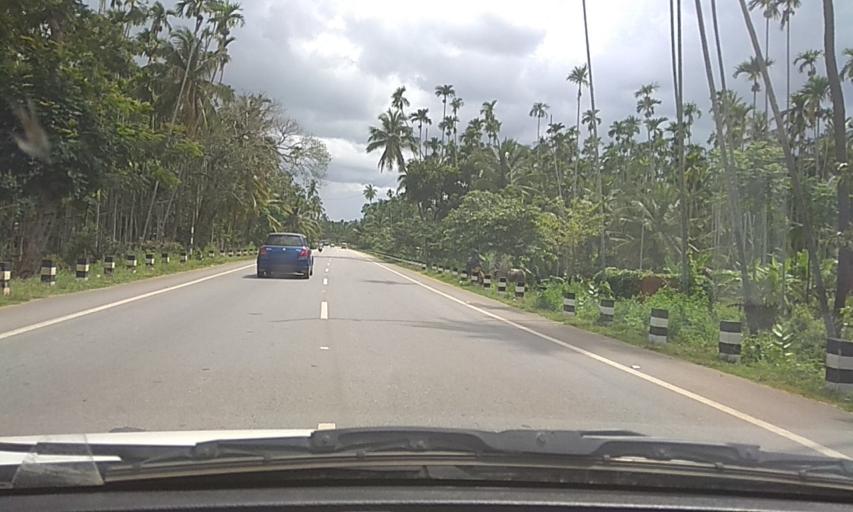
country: IN
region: Karnataka
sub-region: Tumkur
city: Tumkur
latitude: 13.2102
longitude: 77.0539
